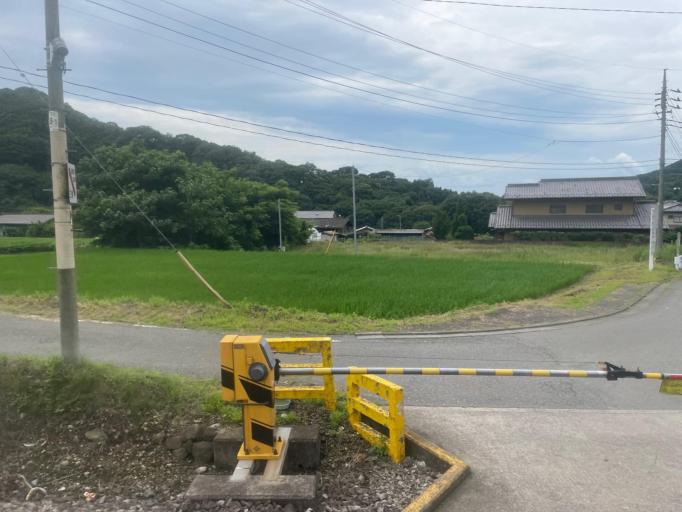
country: JP
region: Gunma
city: Numata
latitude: 36.5707
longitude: 139.0446
